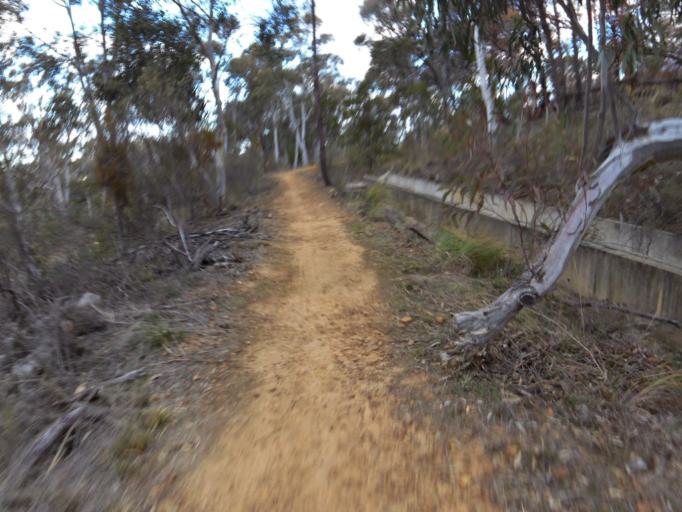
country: AU
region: Australian Capital Territory
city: Acton
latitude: -35.2670
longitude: 149.1095
